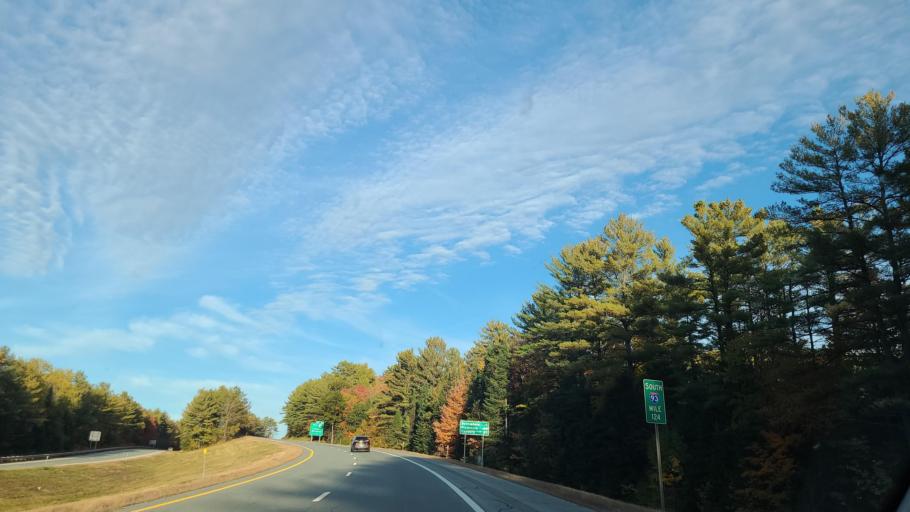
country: US
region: New Hampshire
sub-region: Grafton County
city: Littleton
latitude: 44.3024
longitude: -71.7908
